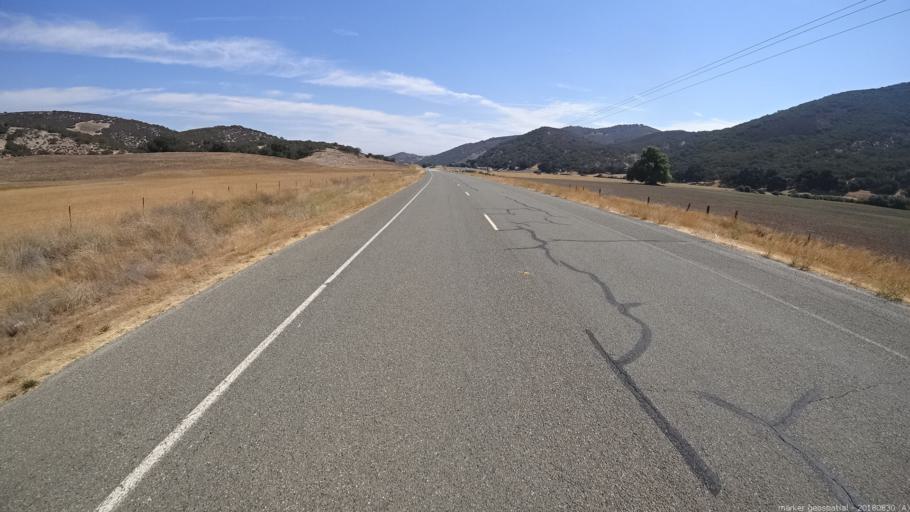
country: US
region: California
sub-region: Monterey County
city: King City
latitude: 36.1017
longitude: -121.1449
